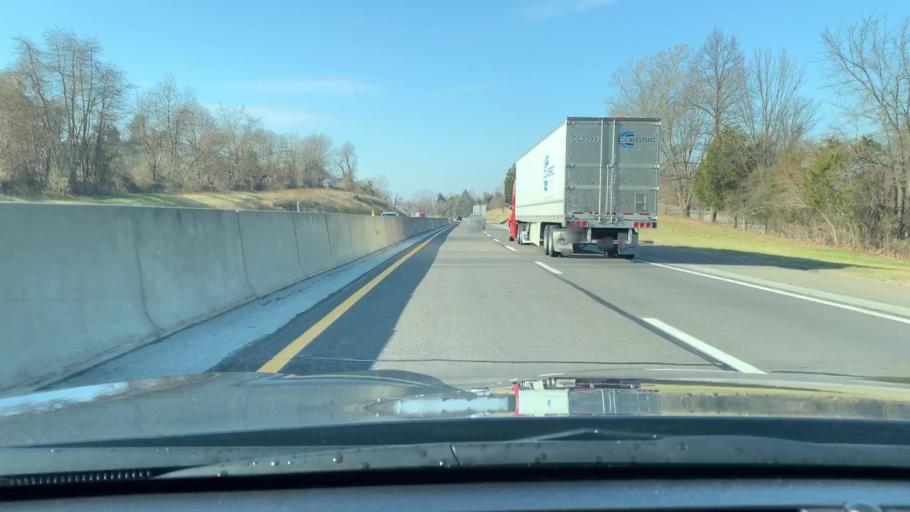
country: US
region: Pennsylvania
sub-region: Chester County
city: Chester Springs
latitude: 40.0653
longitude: -75.6097
